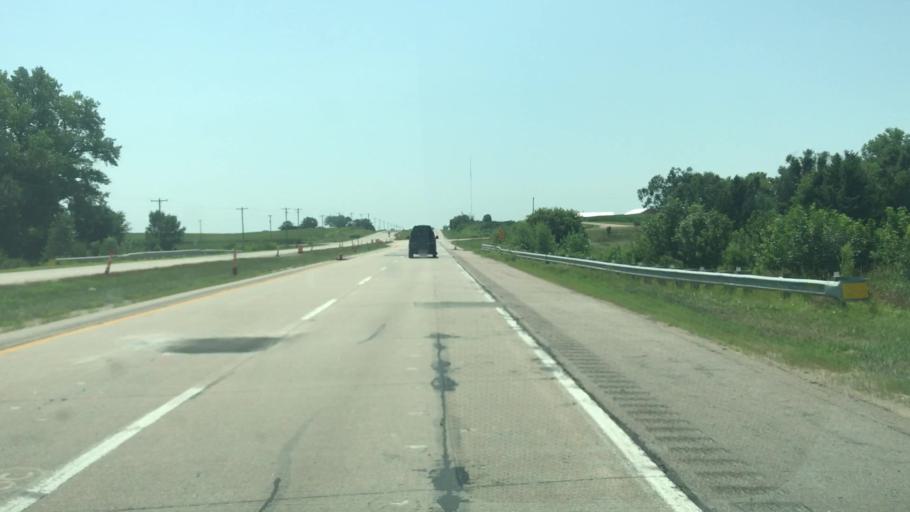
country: US
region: Nebraska
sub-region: Adams County
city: Hastings
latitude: 40.6720
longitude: -98.3823
